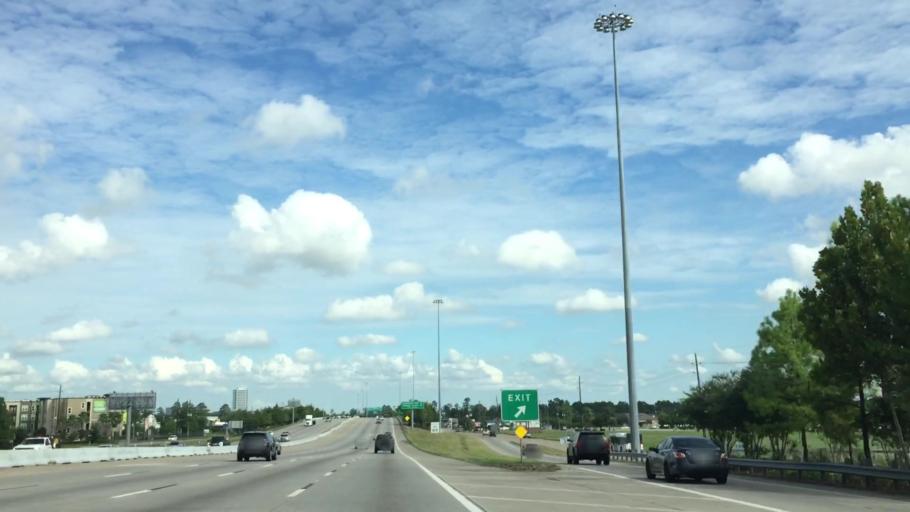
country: US
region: Texas
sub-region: Harris County
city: Oak Cliff Place
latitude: 29.9767
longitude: -95.5643
